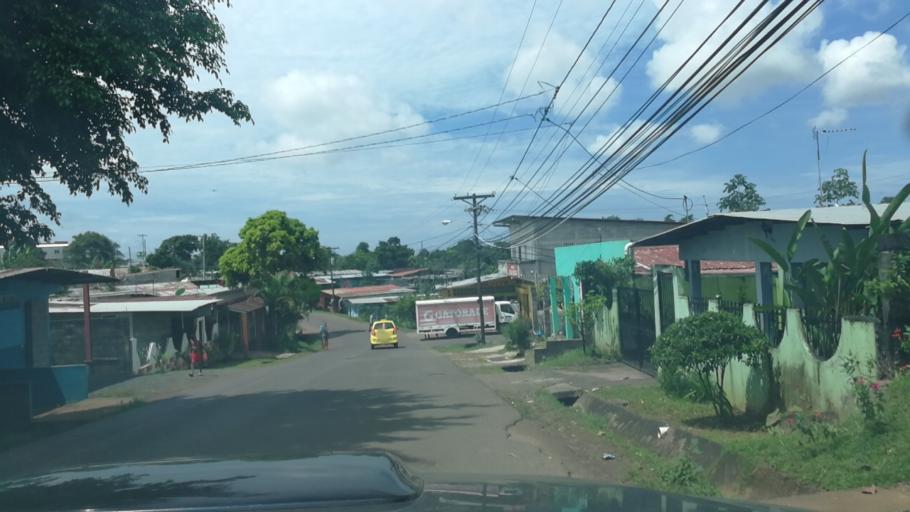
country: PA
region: Panama
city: Tocumen
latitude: 9.0999
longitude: -79.4112
